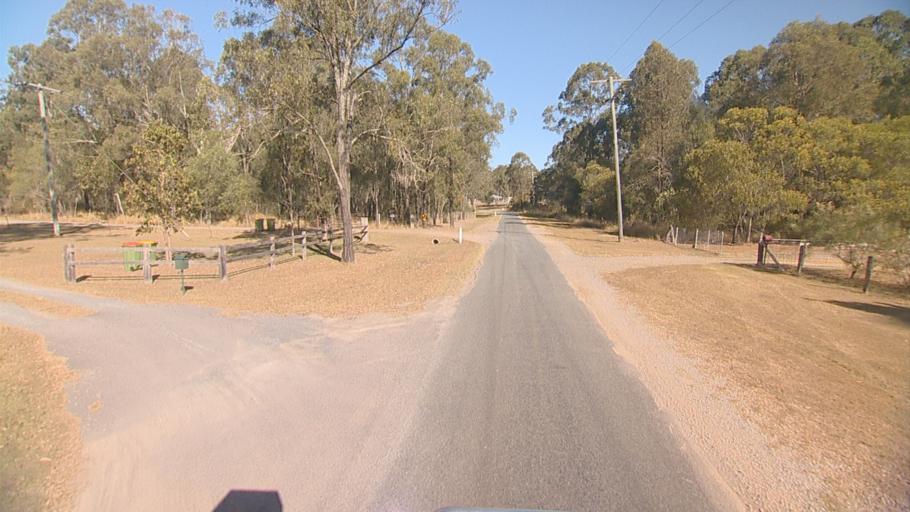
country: AU
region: Queensland
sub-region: Logan
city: Cedar Vale
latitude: -27.8628
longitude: 153.0265
